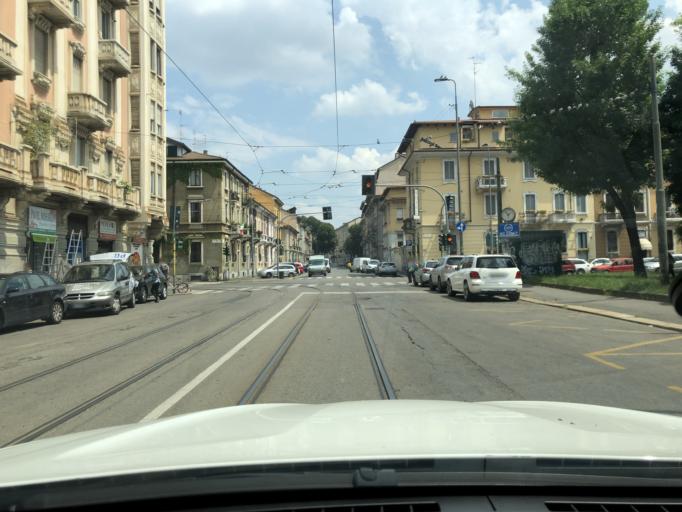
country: IT
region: Lombardy
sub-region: Citta metropolitana di Milano
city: Milano
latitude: 45.4843
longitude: 9.2206
